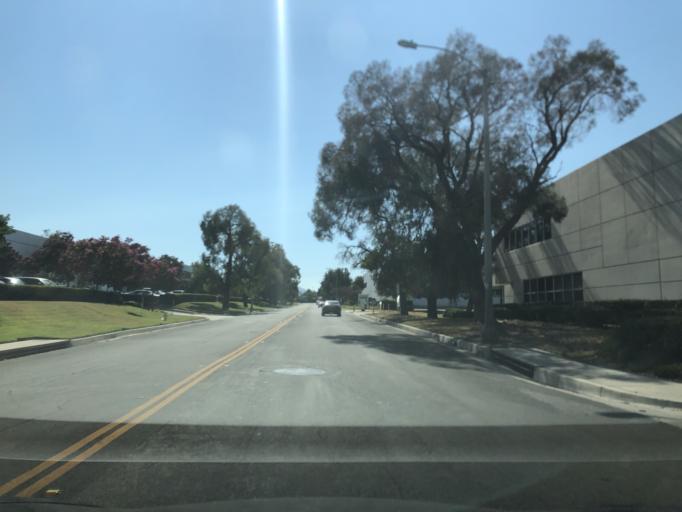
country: US
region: California
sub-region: Riverside County
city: Home Gardens
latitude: 33.8616
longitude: -117.5408
